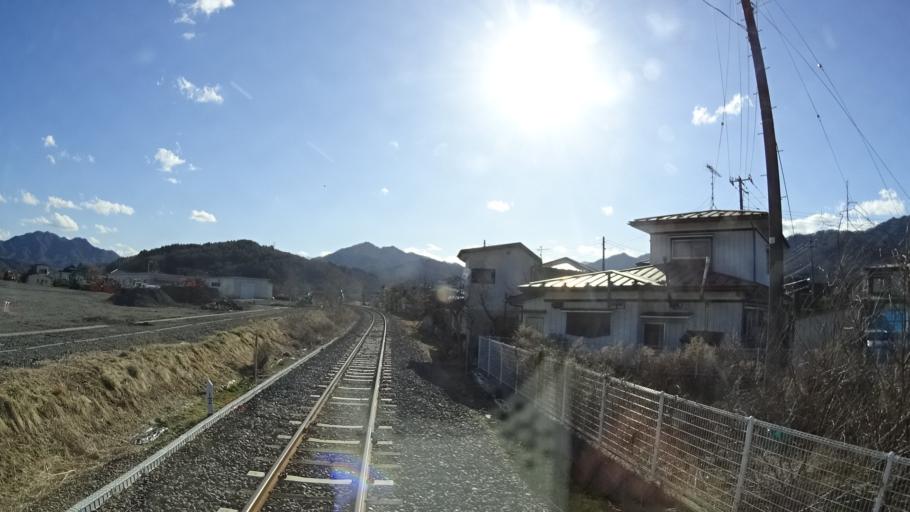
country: JP
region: Iwate
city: Yamada
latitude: 39.5406
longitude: 141.9276
